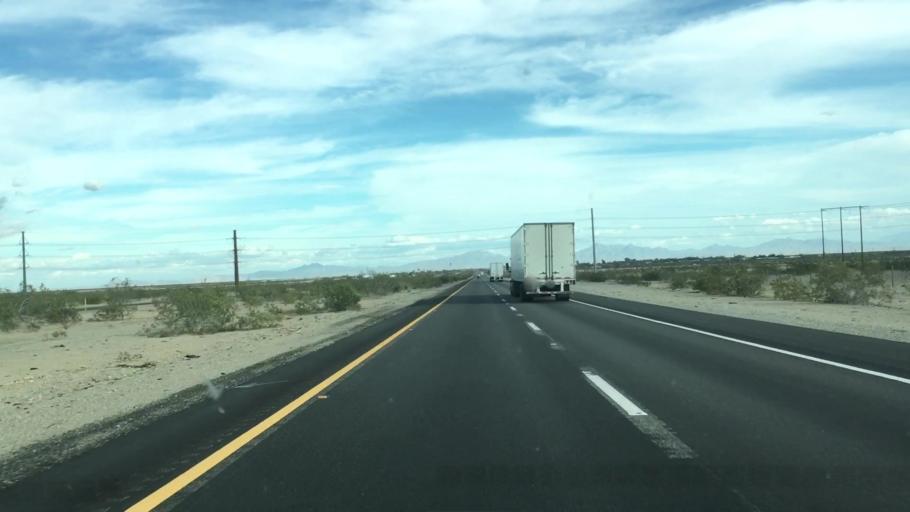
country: US
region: California
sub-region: Riverside County
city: Mesa Verde
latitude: 33.6088
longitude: -114.7575
